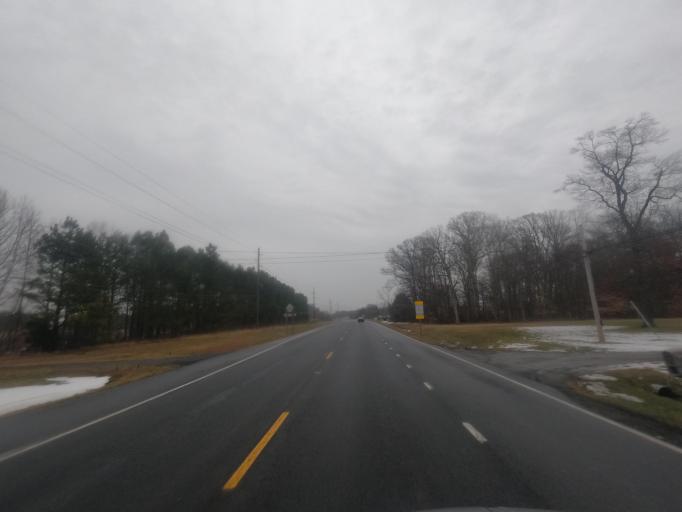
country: US
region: Maryland
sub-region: Dorchester County
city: Cambridge
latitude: 38.5616
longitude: -75.9949
